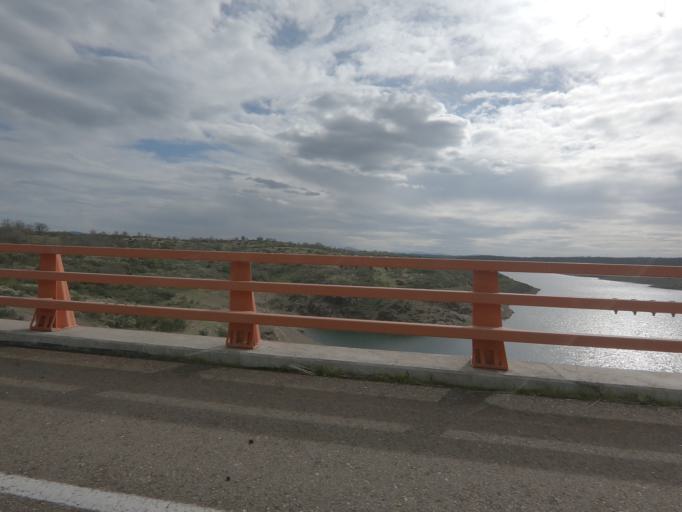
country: ES
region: Castille and Leon
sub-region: Provincia de Salamanca
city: Robleda
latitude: 40.4288
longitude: -6.6007
